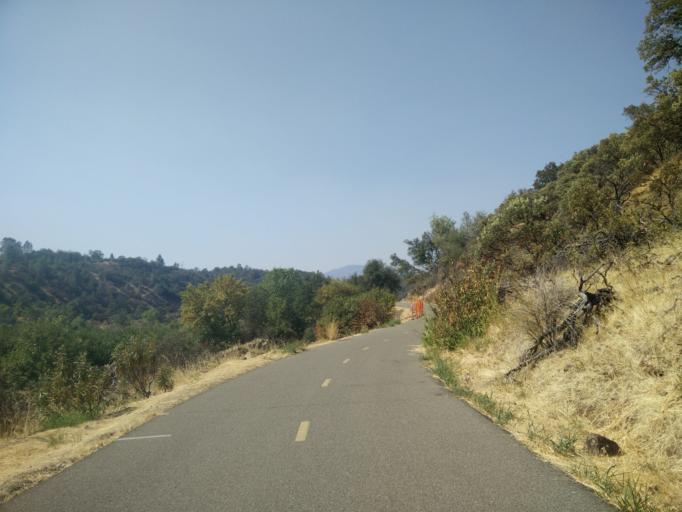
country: US
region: California
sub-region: Shasta County
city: Redding
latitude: 40.5969
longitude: -122.4382
